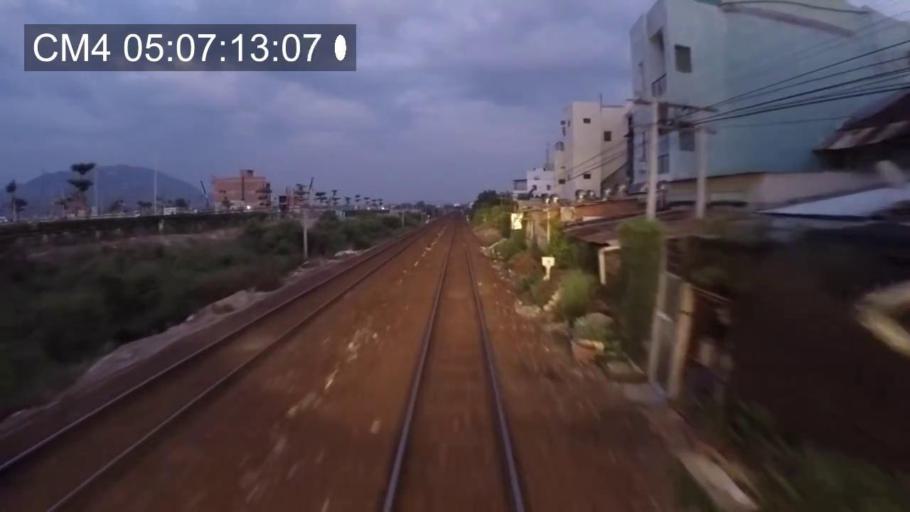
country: VN
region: Khanh Hoa
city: Nha Trang
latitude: 12.2833
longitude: 109.1833
